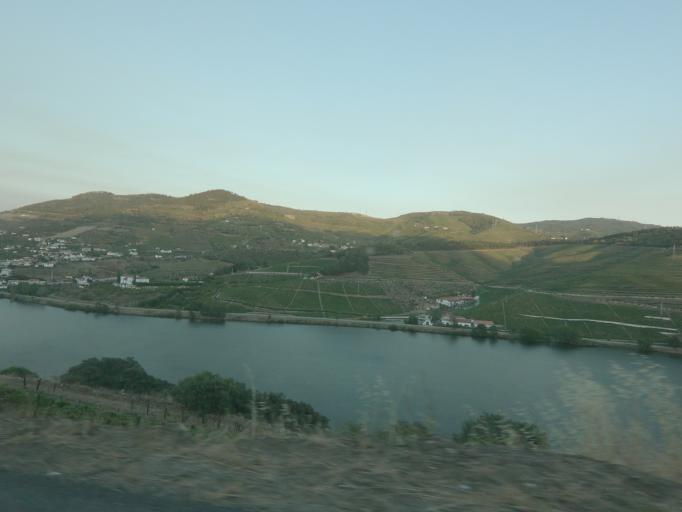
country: PT
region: Viseu
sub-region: Armamar
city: Armamar
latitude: 41.1485
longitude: -7.6919
